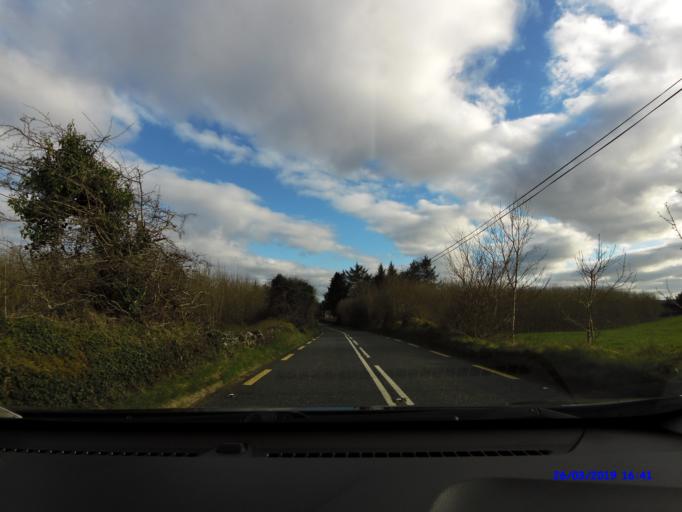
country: IE
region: Connaught
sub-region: Maigh Eo
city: Ballyhaunis
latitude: 53.8722
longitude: -8.7722
